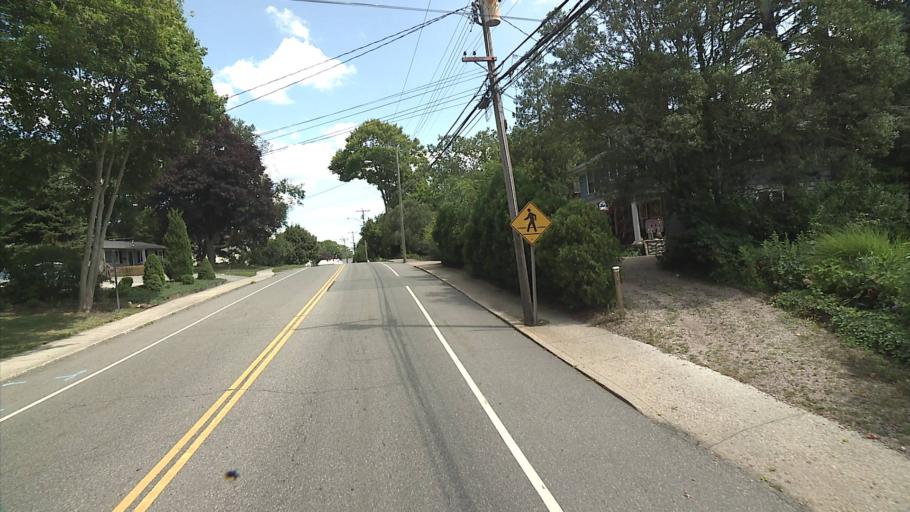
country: US
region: Connecticut
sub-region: New London County
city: Pawcatuck
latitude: 41.3757
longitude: -71.8441
